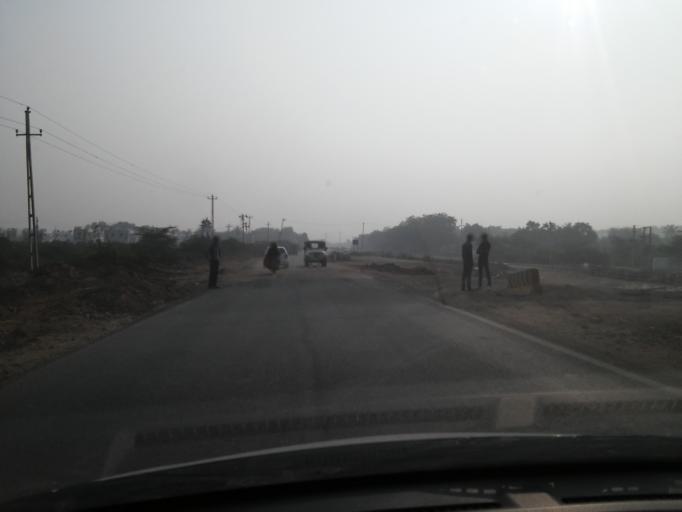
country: IN
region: Gujarat
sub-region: Kachchh
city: Bhuj
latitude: 23.2313
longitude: 69.7520
